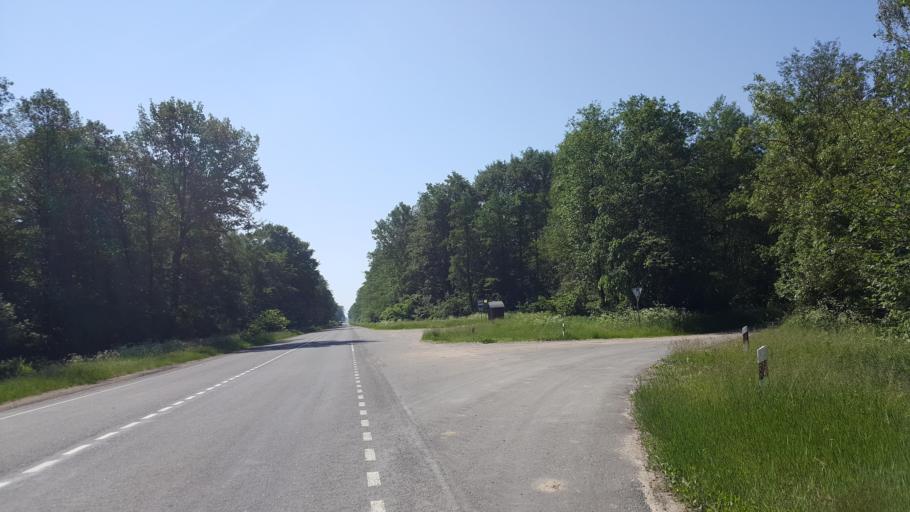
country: BY
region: Brest
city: Zhabinka
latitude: 52.2863
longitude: 23.9443
